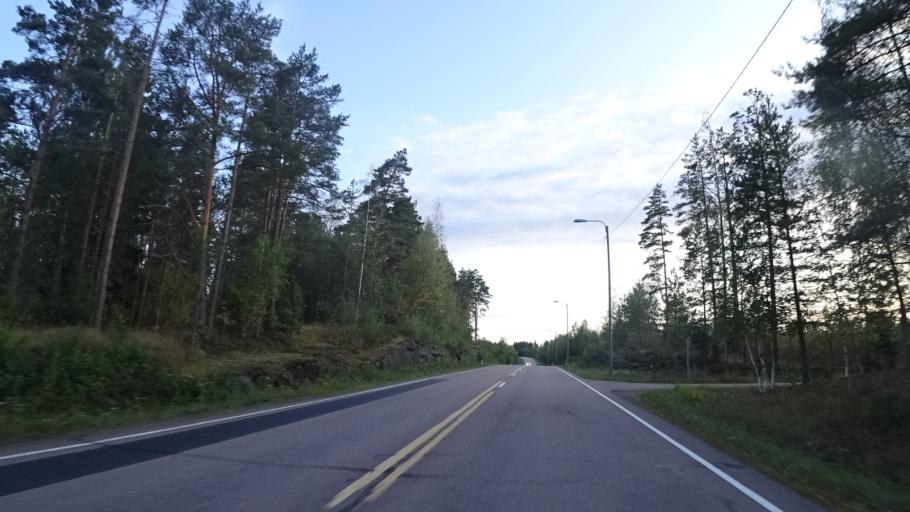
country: FI
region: Kymenlaakso
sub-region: Kotka-Hamina
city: Miehikkaelae
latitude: 60.6483
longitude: 27.8869
